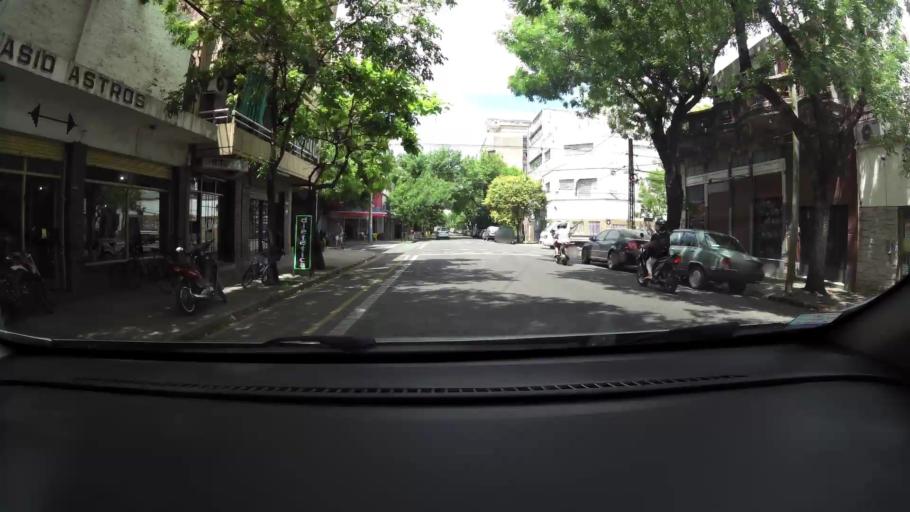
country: AR
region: Santa Fe
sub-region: Departamento de Rosario
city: Rosario
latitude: -32.9737
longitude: -60.6347
